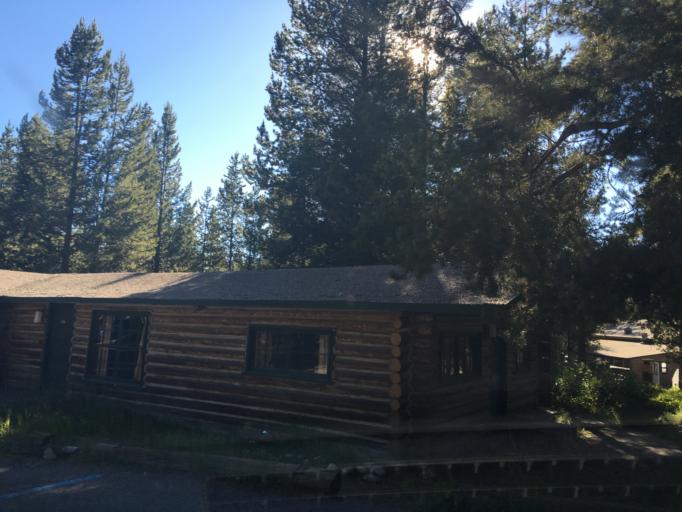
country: US
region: Wyoming
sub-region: Teton County
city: Moose Wilson Road
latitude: 43.9024
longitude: -110.6408
